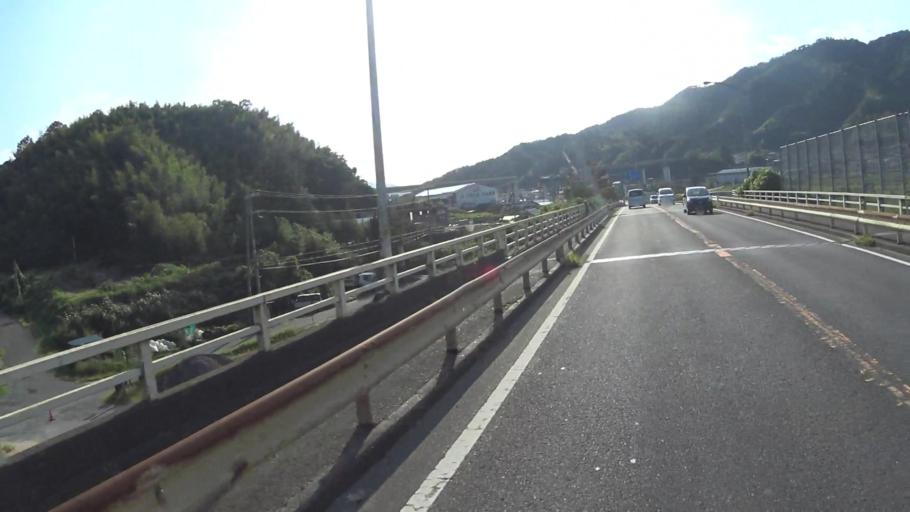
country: JP
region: Kyoto
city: Miyazu
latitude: 35.5527
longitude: 135.1442
